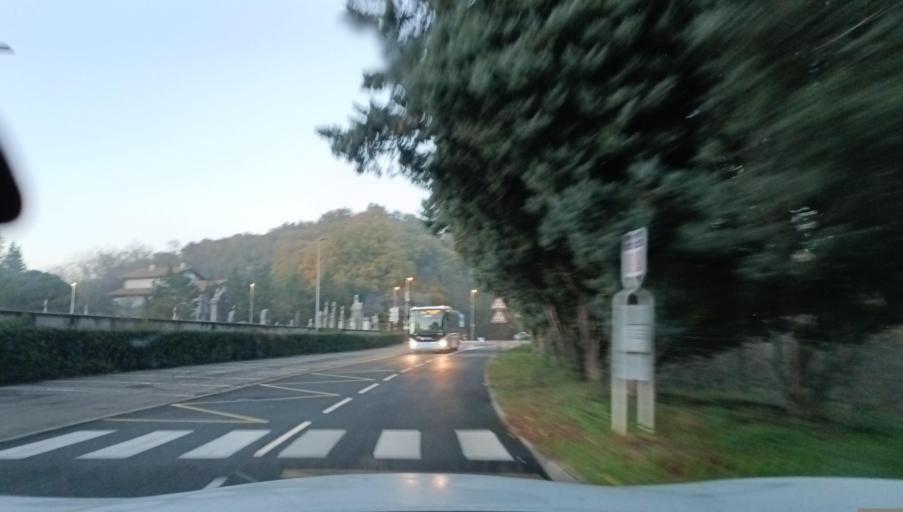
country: FR
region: Rhone-Alpes
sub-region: Departement de l'Isere
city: Chasse-sur-Rhone
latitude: 45.5837
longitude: 4.8028
